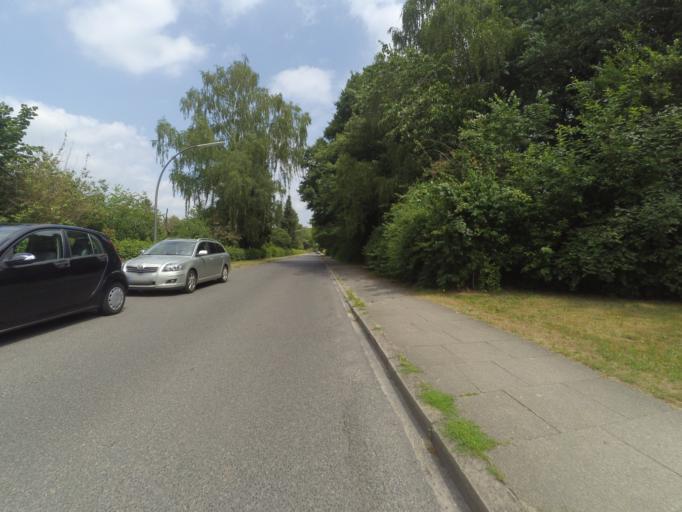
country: DE
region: Hamburg
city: Farmsen-Berne
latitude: 53.6278
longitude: 10.1234
